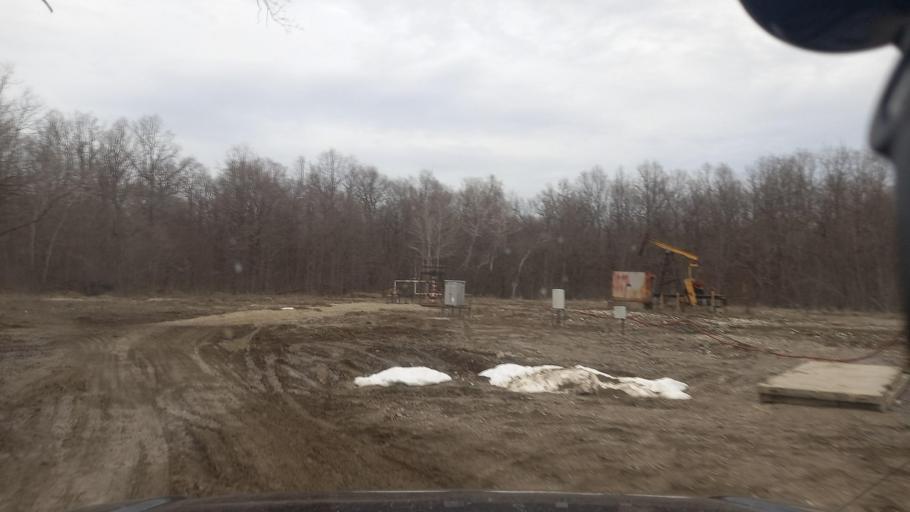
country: RU
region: Krasnodarskiy
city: Novodmitriyevskaya
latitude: 44.7523
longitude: 39.0045
